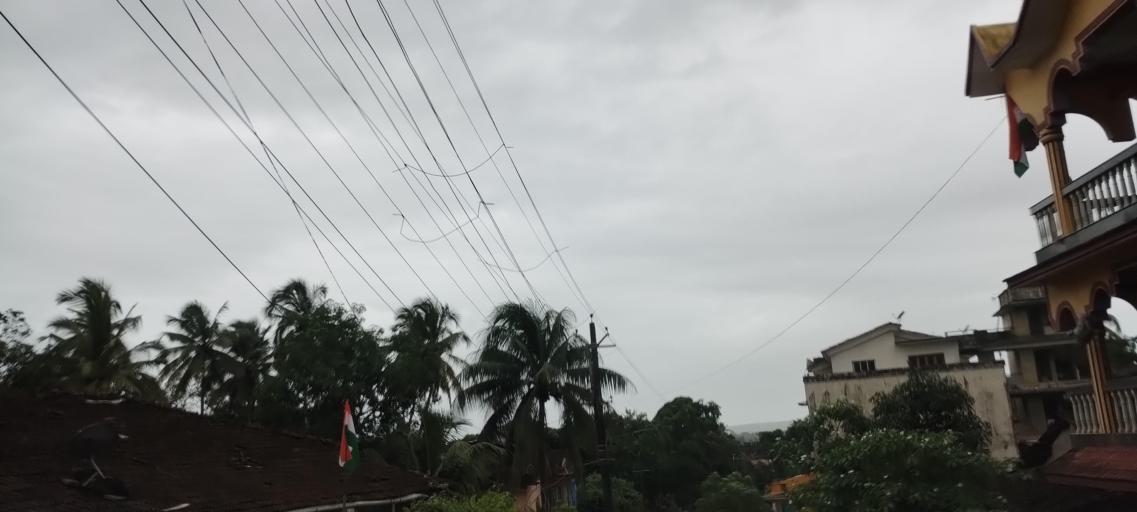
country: IN
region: Goa
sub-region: North Goa
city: Mapuca
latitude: 15.5948
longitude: 73.8062
